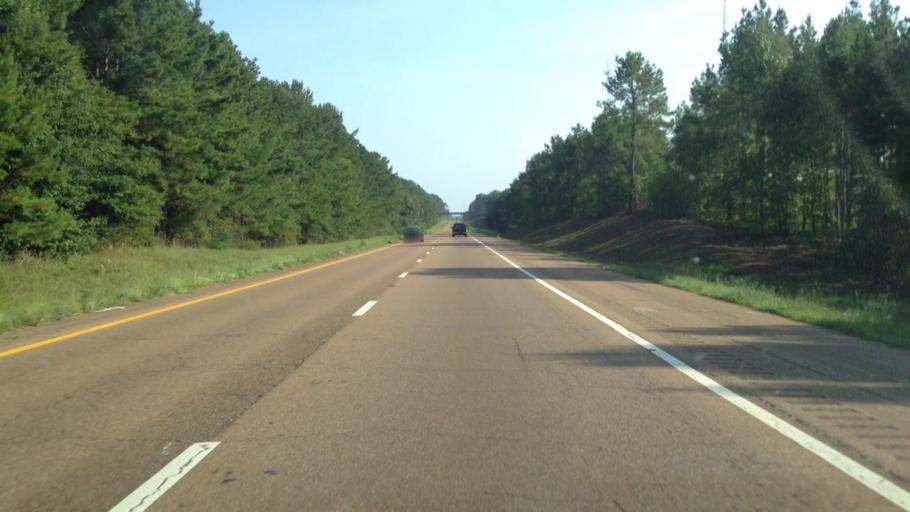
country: US
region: Mississippi
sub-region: Lincoln County
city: Brookhaven
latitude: 31.4694
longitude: -90.4786
